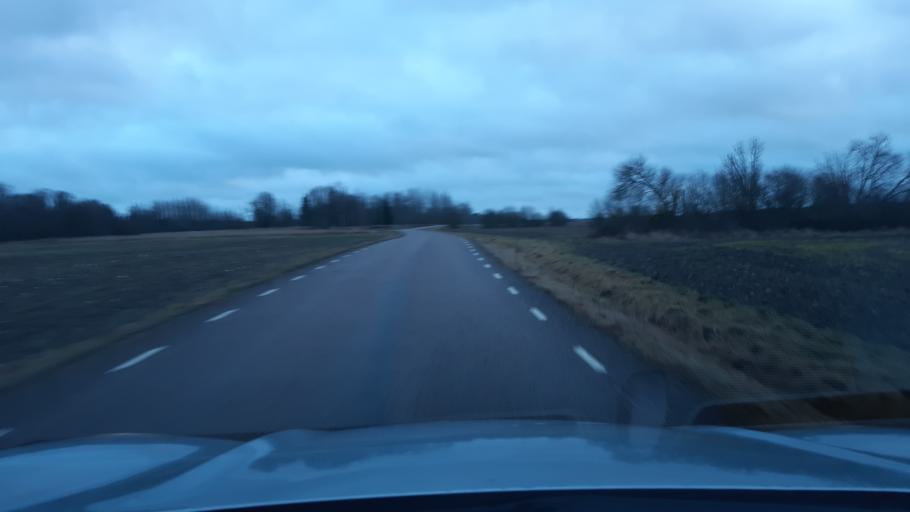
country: EE
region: Raplamaa
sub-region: Rapla vald
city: Rapla
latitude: 59.0080
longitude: 24.7099
